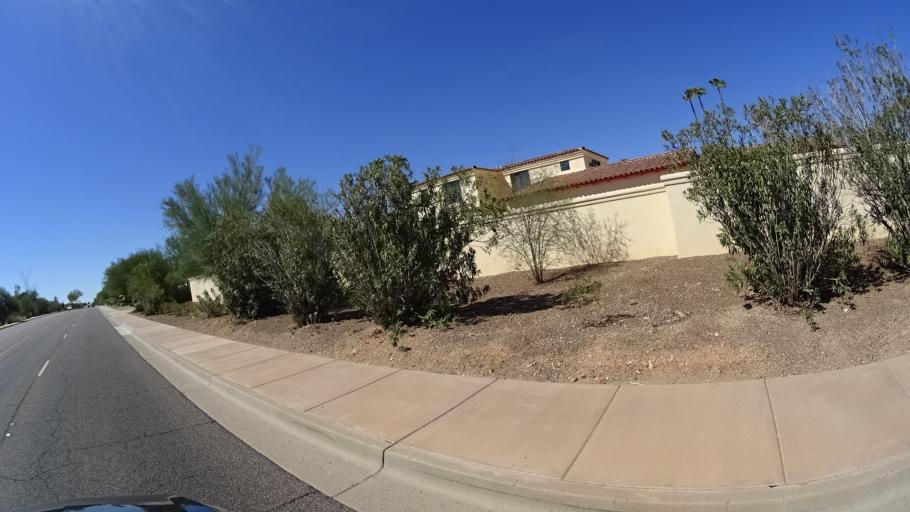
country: US
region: Arizona
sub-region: Maricopa County
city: Paradise Valley
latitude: 33.5311
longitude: -111.9788
